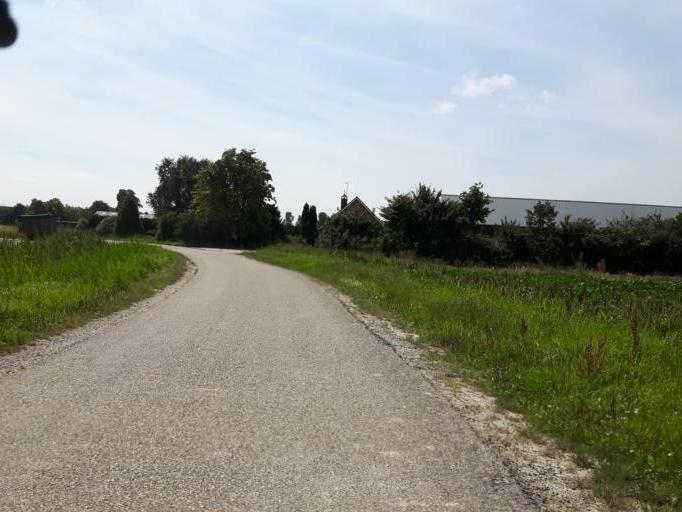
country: NL
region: Zeeland
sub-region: Gemeente Goes
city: Goes
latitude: 51.4755
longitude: 3.8384
